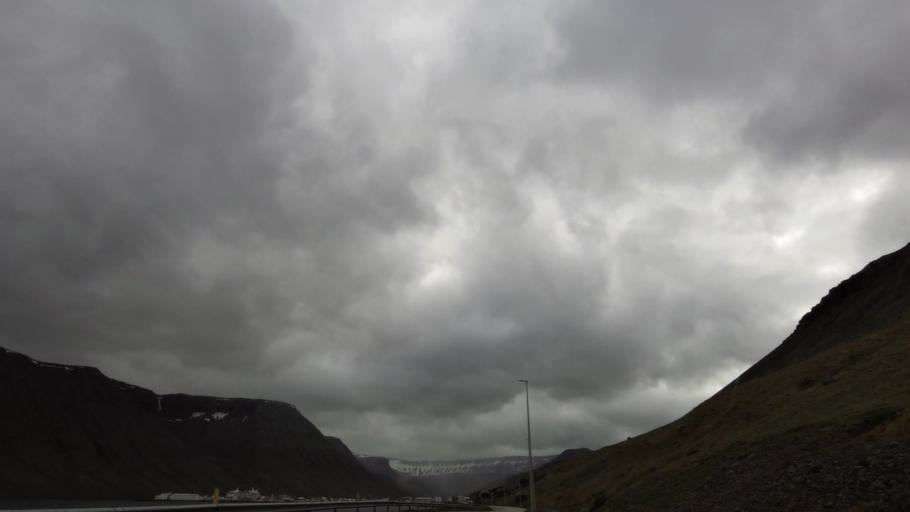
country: IS
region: Westfjords
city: Isafjoerdur
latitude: 66.0880
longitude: -23.1177
